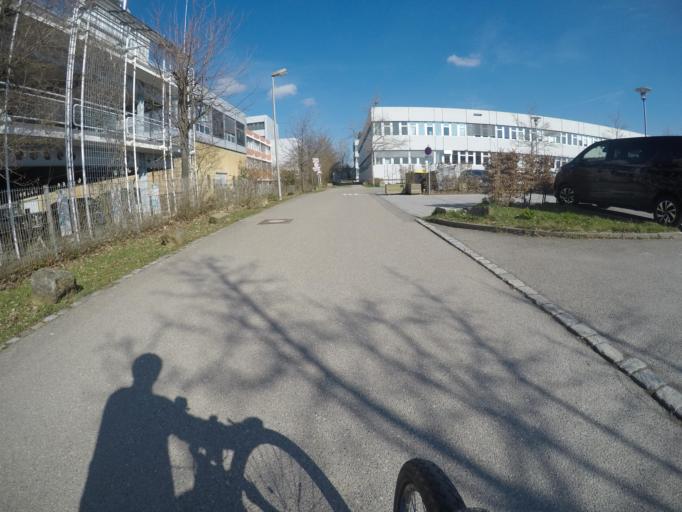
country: DE
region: Baden-Wuerttemberg
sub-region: Regierungsbezirk Stuttgart
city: Gerlingen
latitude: 48.7410
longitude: 9.1002
